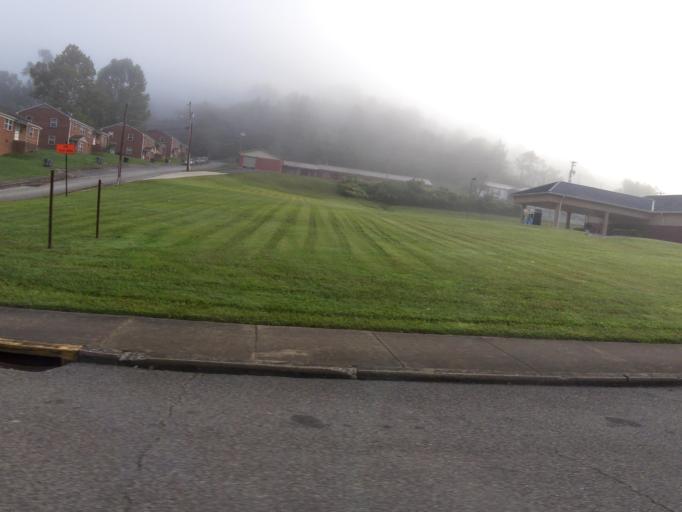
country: US
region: Tennessee
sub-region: Campbell County
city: Jellico
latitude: 36.5837
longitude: -84.1189
